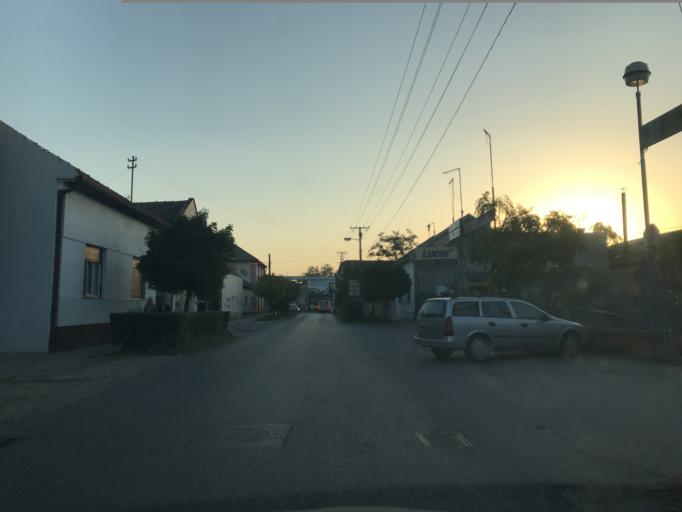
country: RS
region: Autonomna Pokrajina Vojvodina
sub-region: Juznobacki Okrug
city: Novi Sad
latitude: 45.2727
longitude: 19.8398
